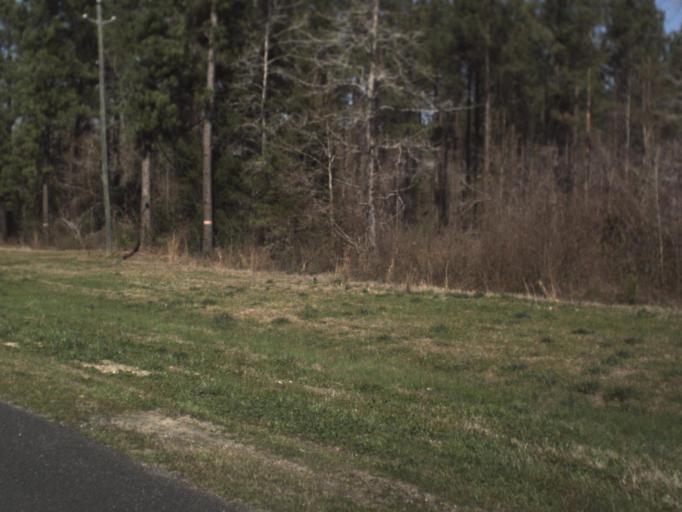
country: US
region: Florida
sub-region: Jackson County
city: Graceville
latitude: 30.9627
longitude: -85.4050
